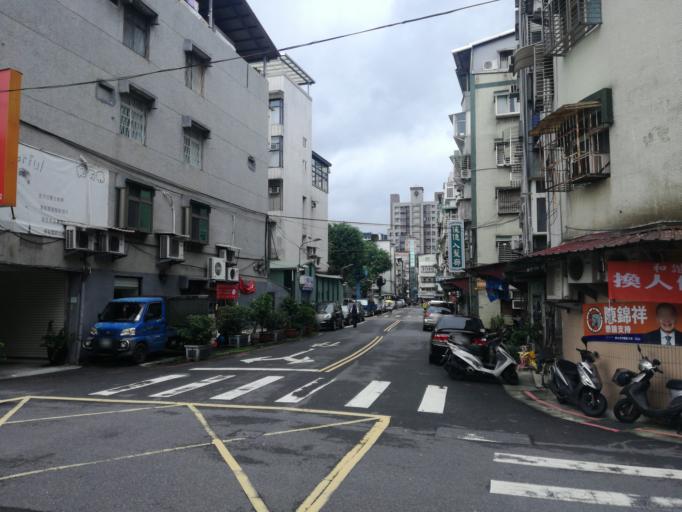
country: TW
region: Taipei
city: Taipei
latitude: 24.9843
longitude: 121.5628
